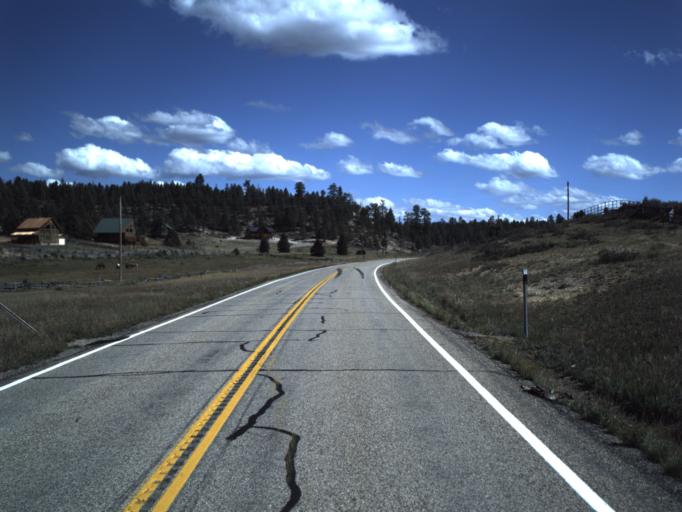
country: US
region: Utah
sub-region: Garfield County
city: Panguitch
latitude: 37.4947
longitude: -112.5780
